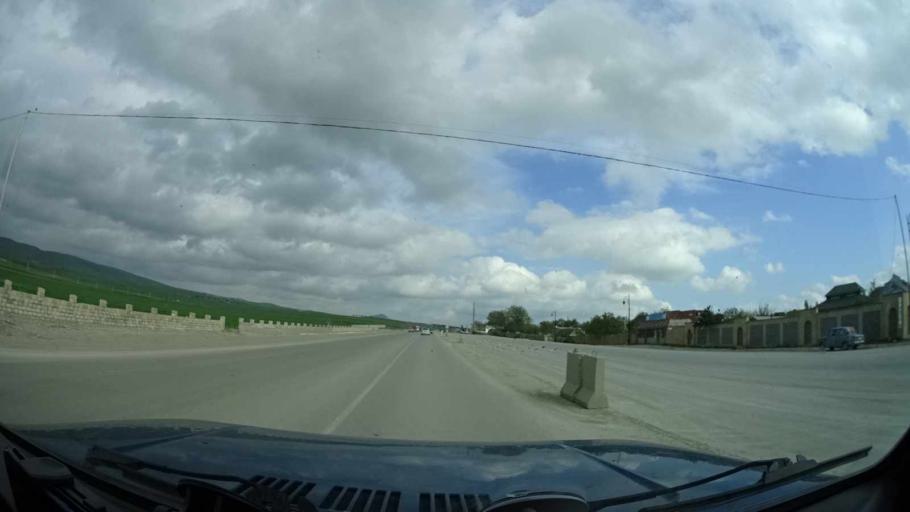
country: AZ
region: Samaxi
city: Shamakhi
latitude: 40.5903
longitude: 48.7077
